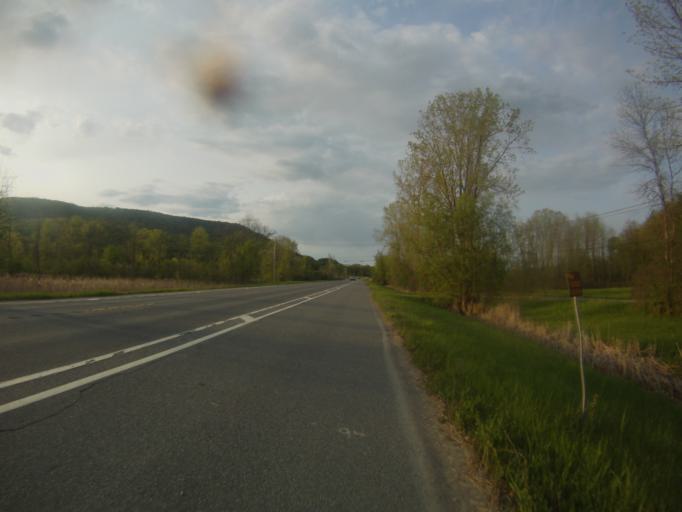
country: US
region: New York
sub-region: Essex County
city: Ticonderoga
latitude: 43.9051
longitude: -73.4262
